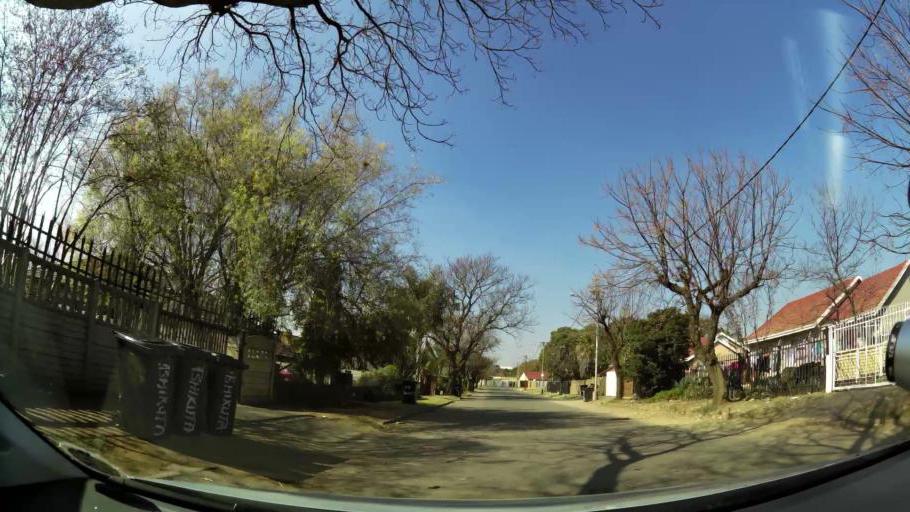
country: ZA
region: Gauteng
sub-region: City of Johannesburg Metropolitan Municipality
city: Modderfontein
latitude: -26.1154
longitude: 28.2307
